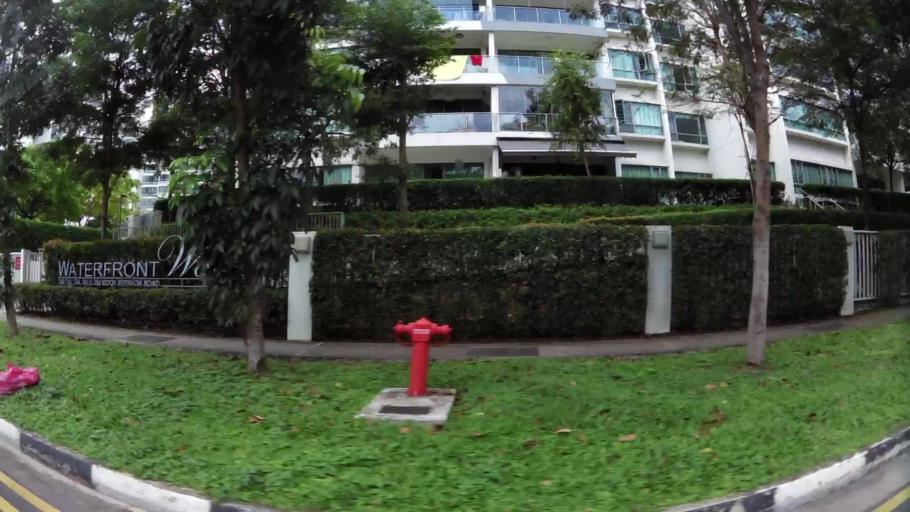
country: SG
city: Singapore
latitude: 1.3382
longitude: 103.9303
